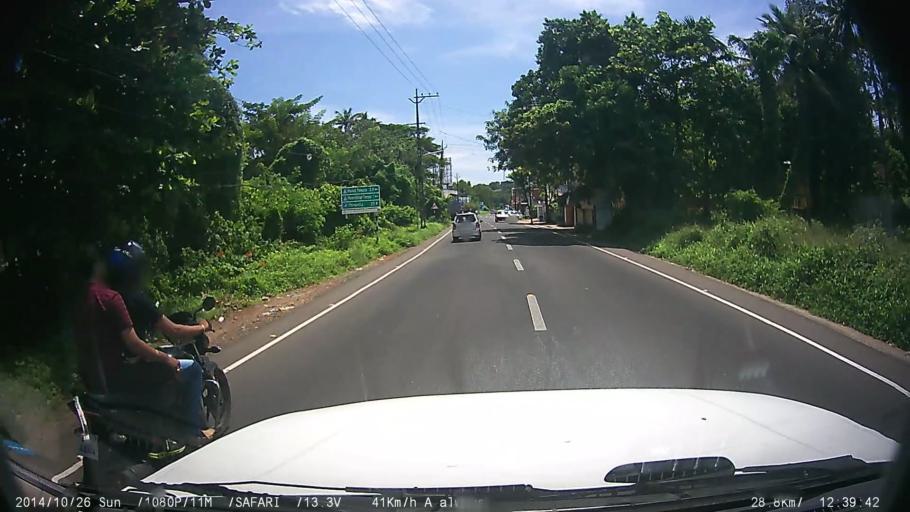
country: IN
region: Kerala
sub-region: Kottayam
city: Kottayam
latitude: 9.5606
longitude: 76.5156
